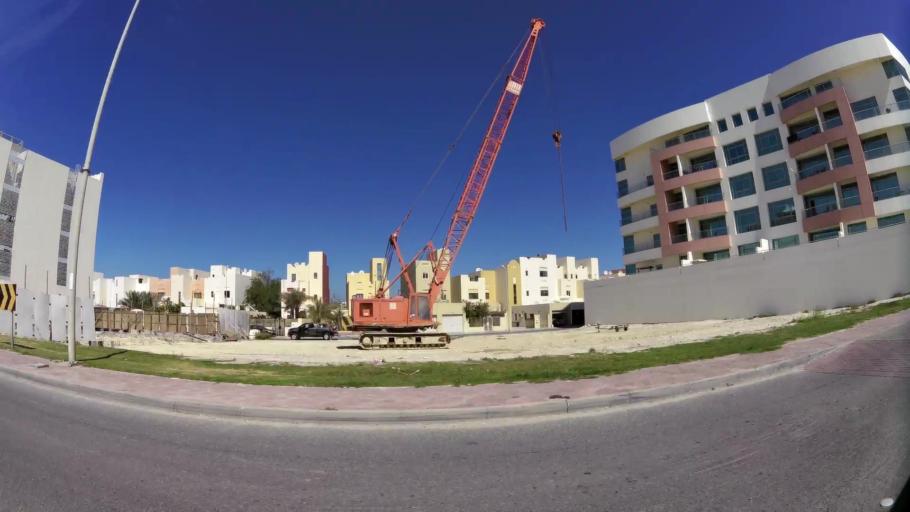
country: BH
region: Muharraq
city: Al Hadd
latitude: 26.2949
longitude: 50.6588
